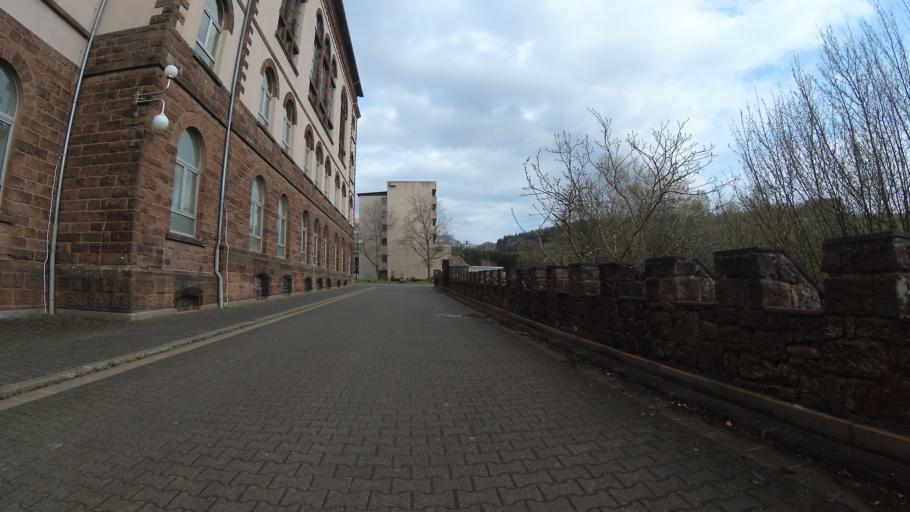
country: DE
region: Saarland
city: Sankt Wendel
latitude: 49.4637
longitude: 7.1923
